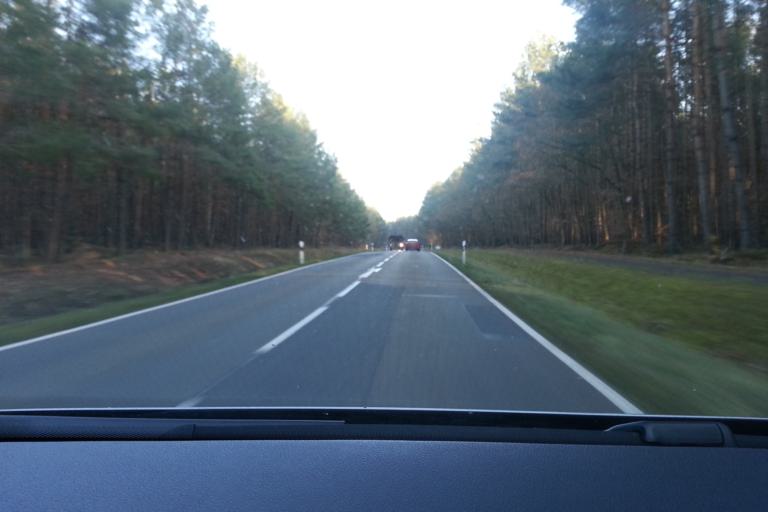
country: DE
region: Mecklenburg-Vorpommern
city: Torgelow
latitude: 53.6359
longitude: 13.9637
